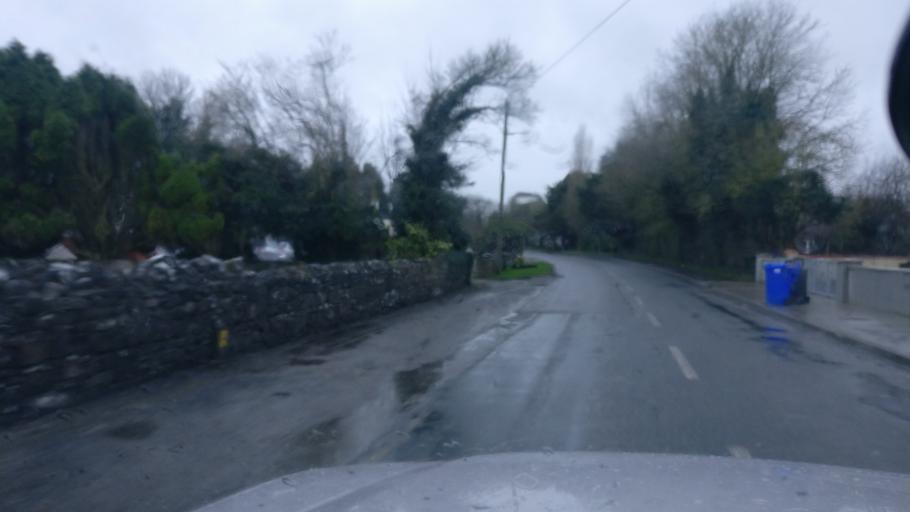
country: IE
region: Connaught
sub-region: County Galway
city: Ballinasloe
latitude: 53.2393
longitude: -8.1730
